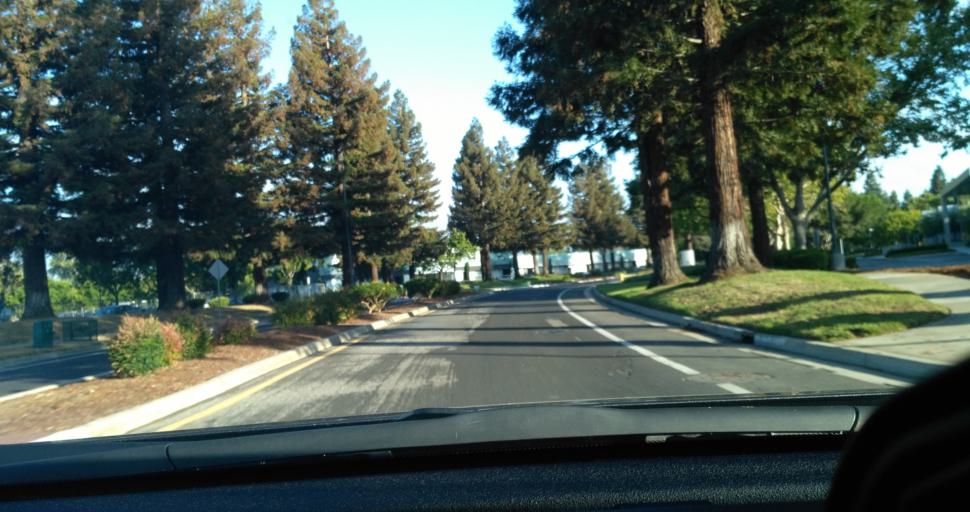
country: US
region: California
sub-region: Santa Clara County
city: Santa Clara
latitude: 37.3899
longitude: -121.9361
